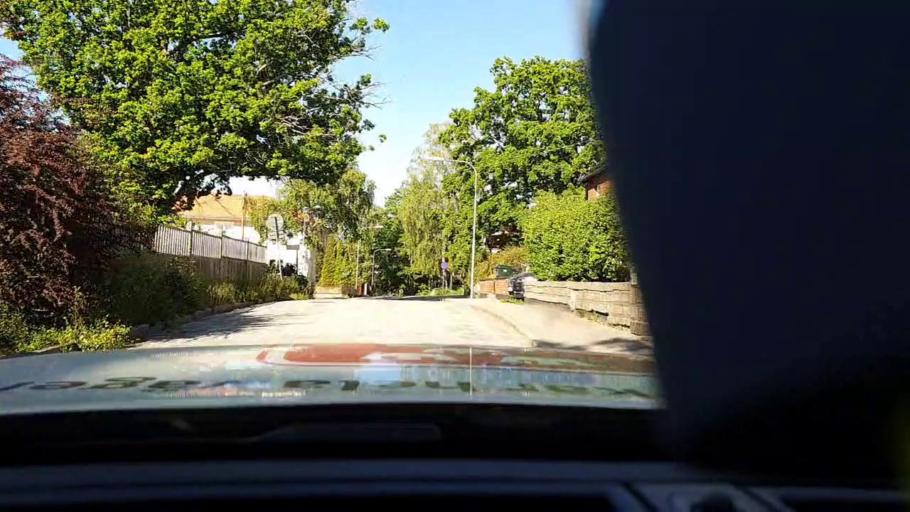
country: SE
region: Stockholm
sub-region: Stockholms Kommun
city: Arsta
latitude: 59.2691
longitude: 18.0251
